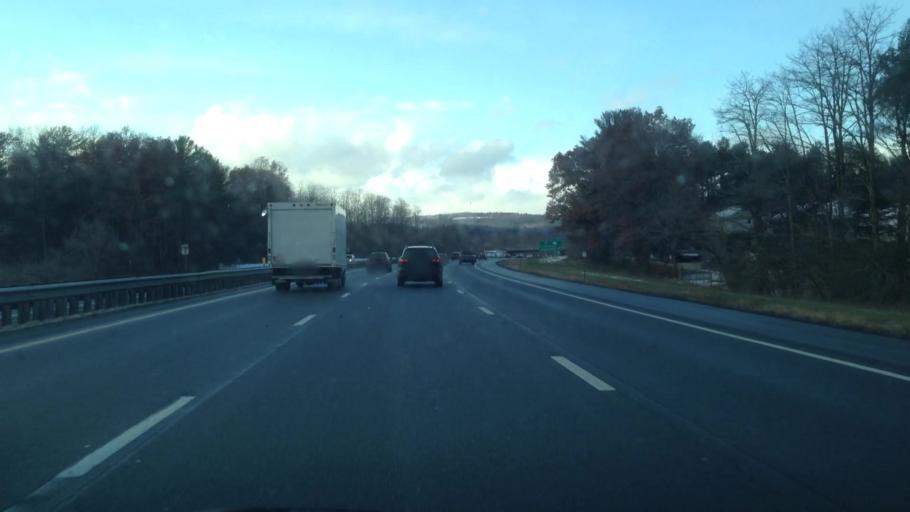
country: US
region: New York
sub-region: Schenectady County
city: Rotterdam
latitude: 42.7828
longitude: -74.0089
